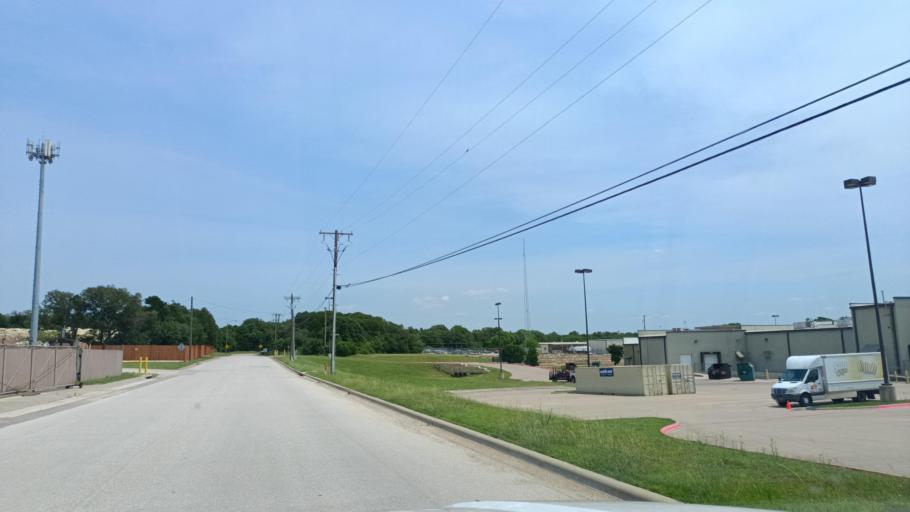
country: US
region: Texas
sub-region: Bell County
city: Temple
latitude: 31.0945
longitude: -97.3859
